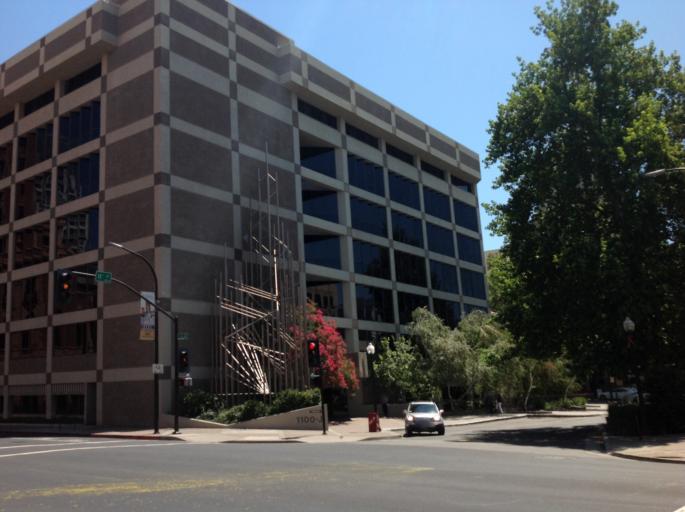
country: US
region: California
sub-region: Sacramento County
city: Sacramento
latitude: 38.5799
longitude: -121.4920
